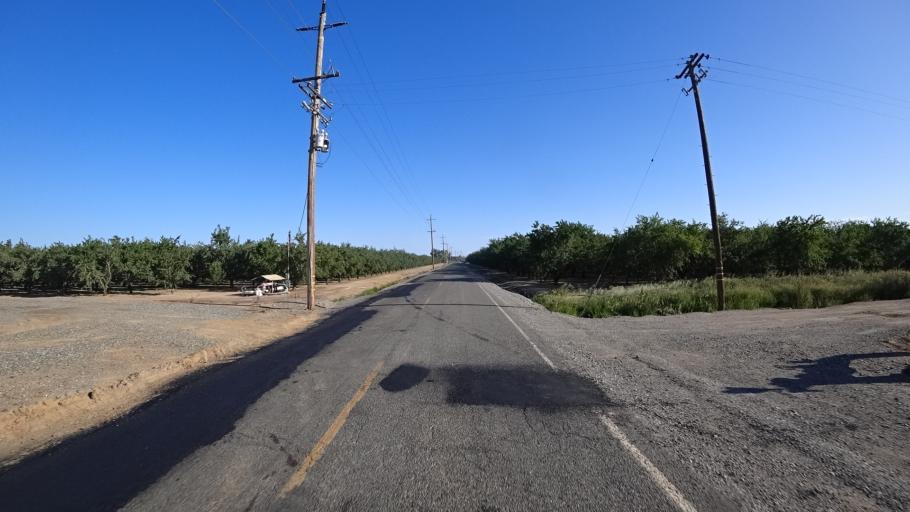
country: US
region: California
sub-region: Glenn County
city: Orland
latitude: 39.7072
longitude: -122.1783
